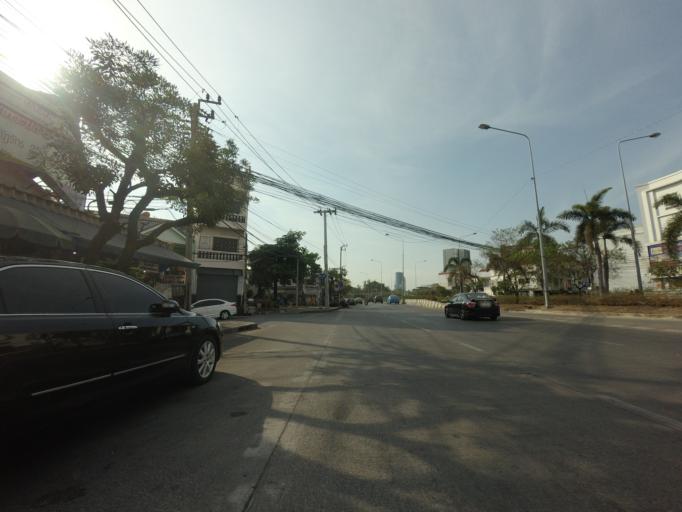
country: TH
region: Bangkok
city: Bang Kapi
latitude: 13.7543
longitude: 100.6301
